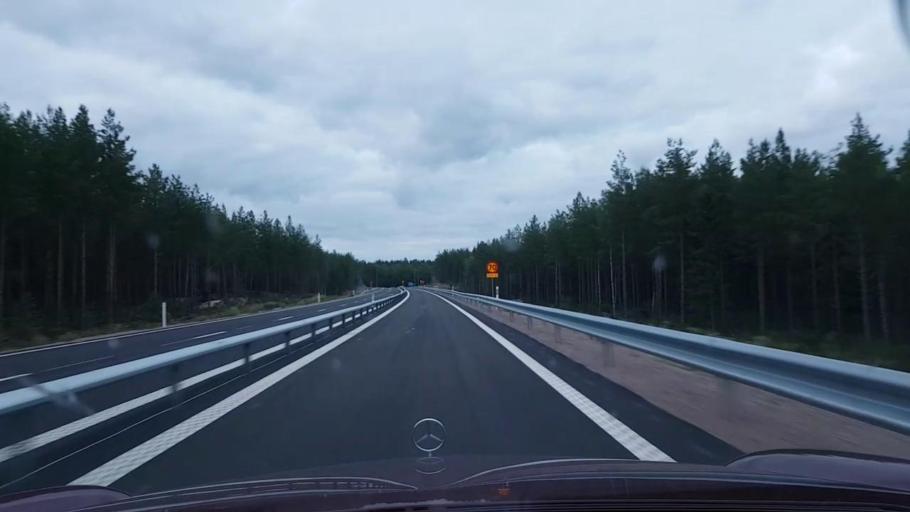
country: SE
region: Vaestmanland
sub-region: Surahammars Kommun
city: Surahammar
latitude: 59.6871
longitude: 16.2502
